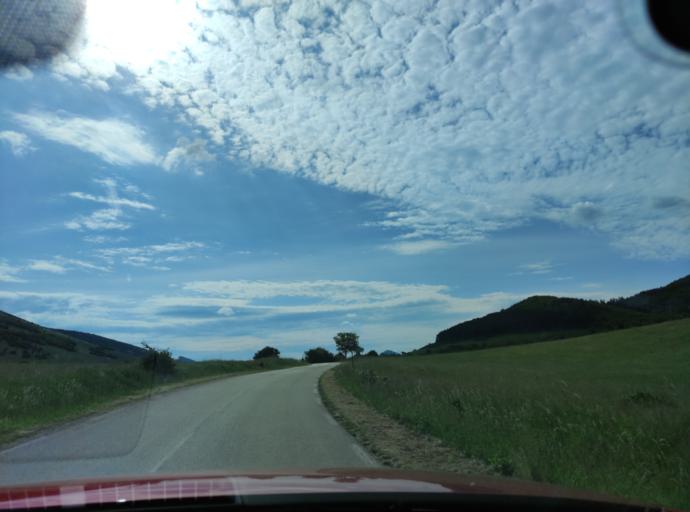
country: BG
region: Vidin
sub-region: Obshtina Belogradchik
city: Belogradchik
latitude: 43.5187
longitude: 22.7263
